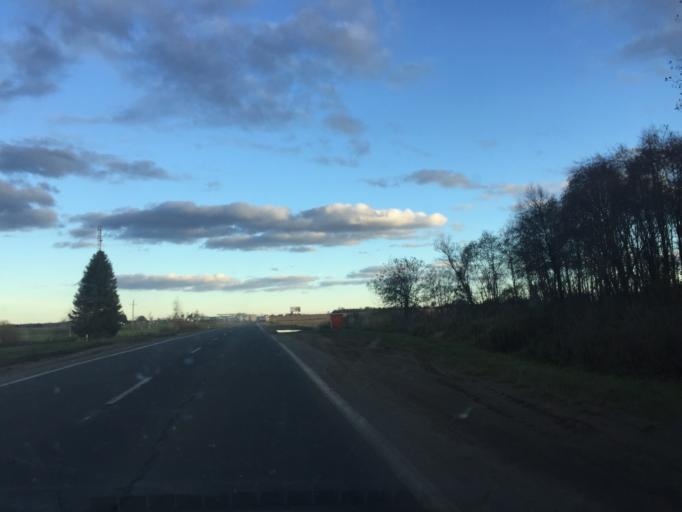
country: BY
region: Vitebsk
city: Myory
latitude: 55.8176
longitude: 27.6566
